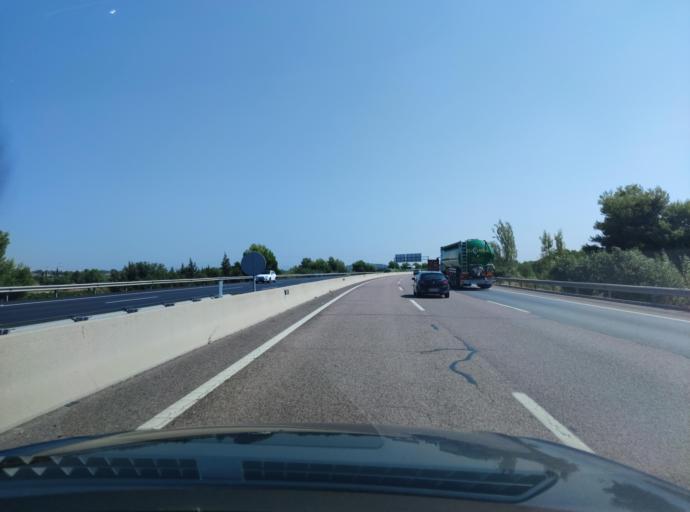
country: ES
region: Valencia
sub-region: Provincia de Valencia
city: Ribarroja
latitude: 39.4901
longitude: -0.5400
